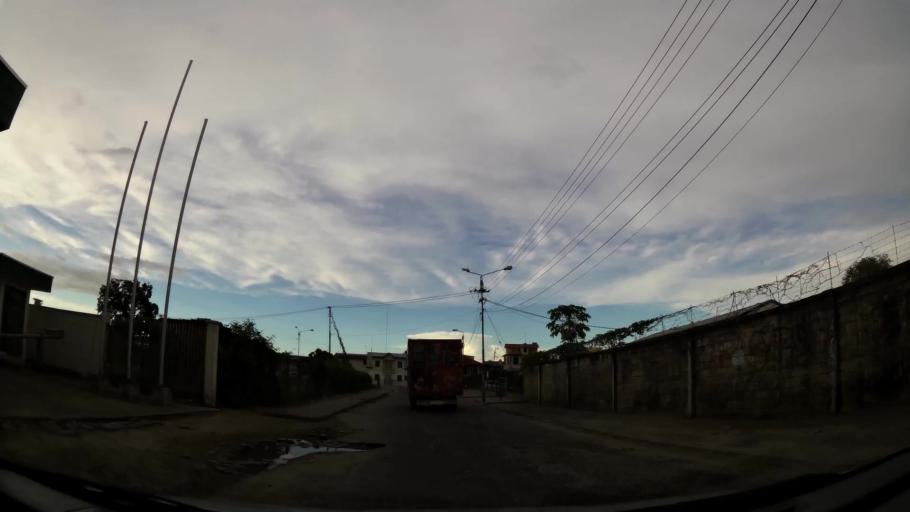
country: SR
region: Paramaribo
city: Paramaribo
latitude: 5.8295
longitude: -55.1529
